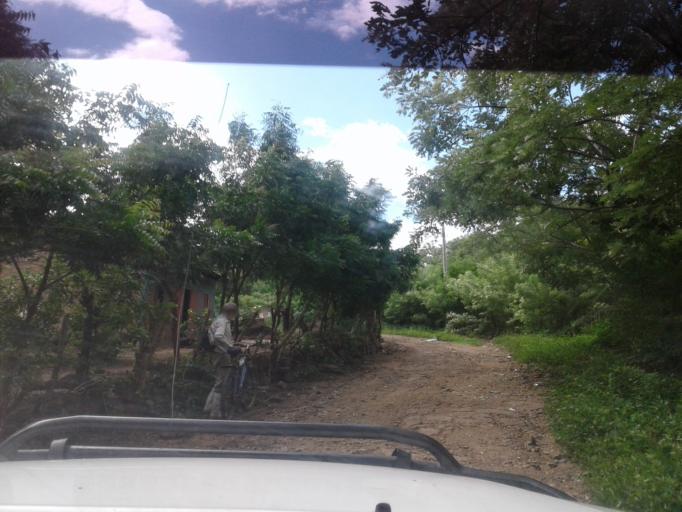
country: NI
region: Leon
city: Santa Rosa del Penon
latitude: 12.8545
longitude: -86.2253
